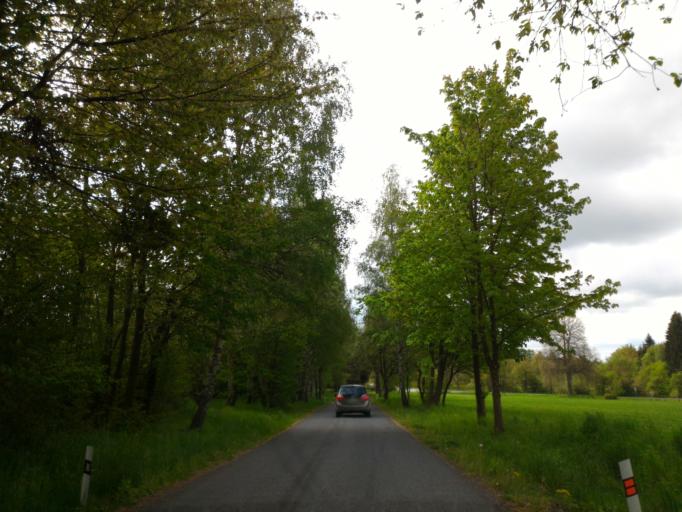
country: CZ
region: Vysocina
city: Ledec nad Sazavou
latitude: 49.6137
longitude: 15.2853
